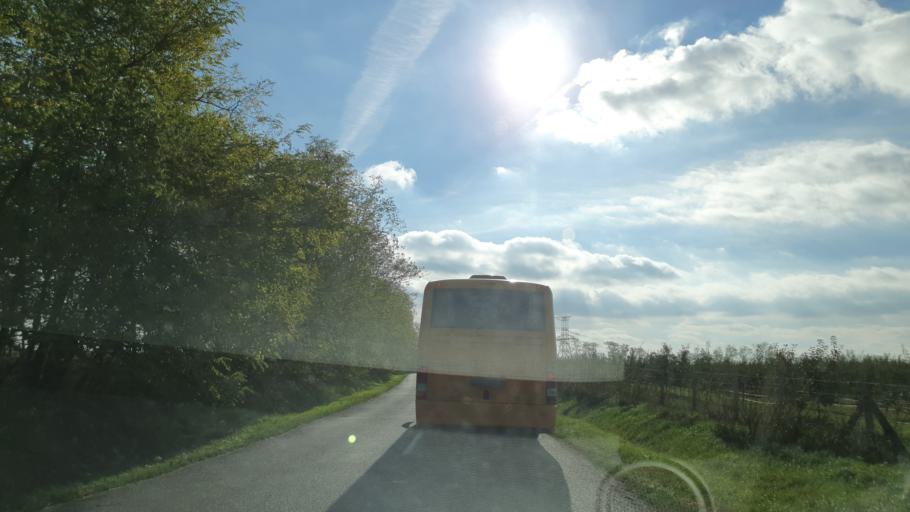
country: HU
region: Szabolcs-Szatmar-Bereg
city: Gyulahaza
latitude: 48.1217
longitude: 22.0888
